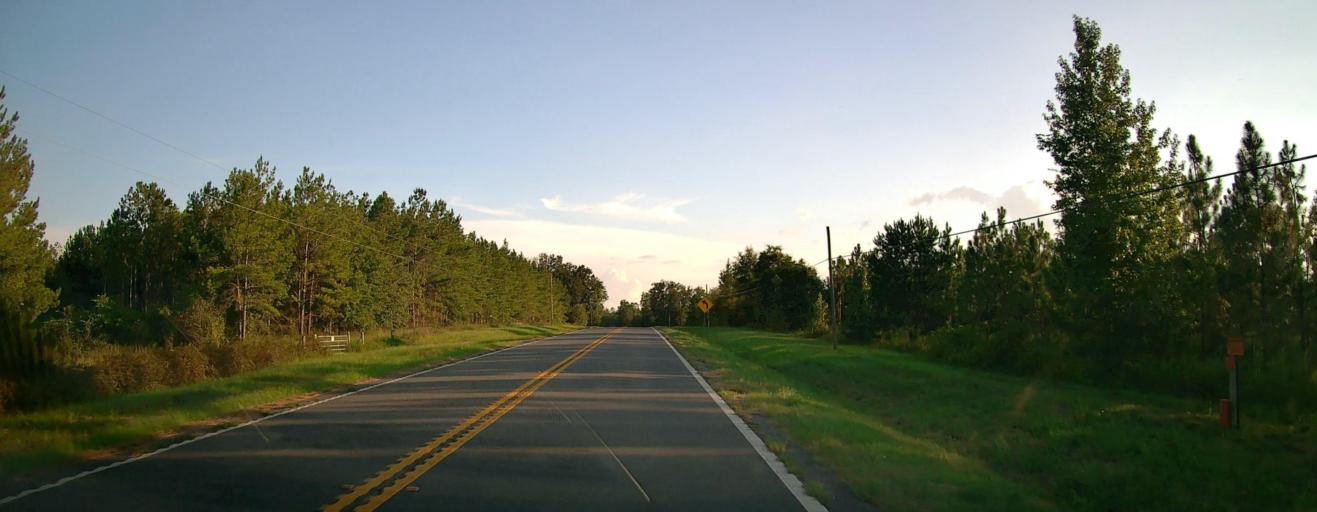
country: US
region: Georgia
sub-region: Taylor County
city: Reynolds
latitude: 32.6320
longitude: -84.1010
